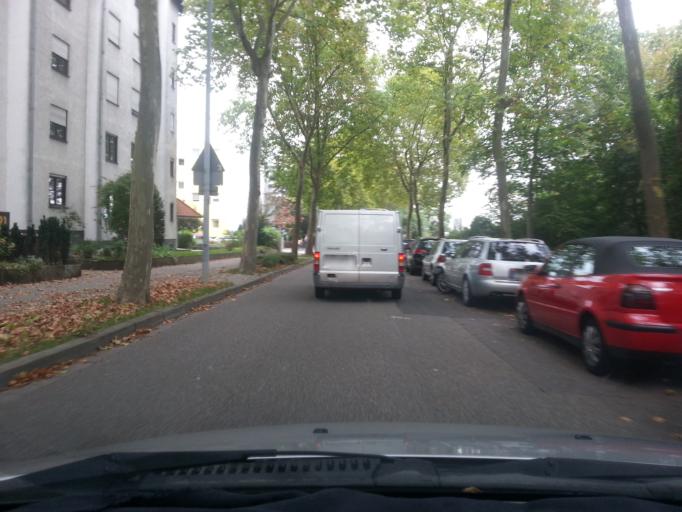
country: DE
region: Rheinland-Pfalz
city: Speyer
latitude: 49.3216
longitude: 8.4275
